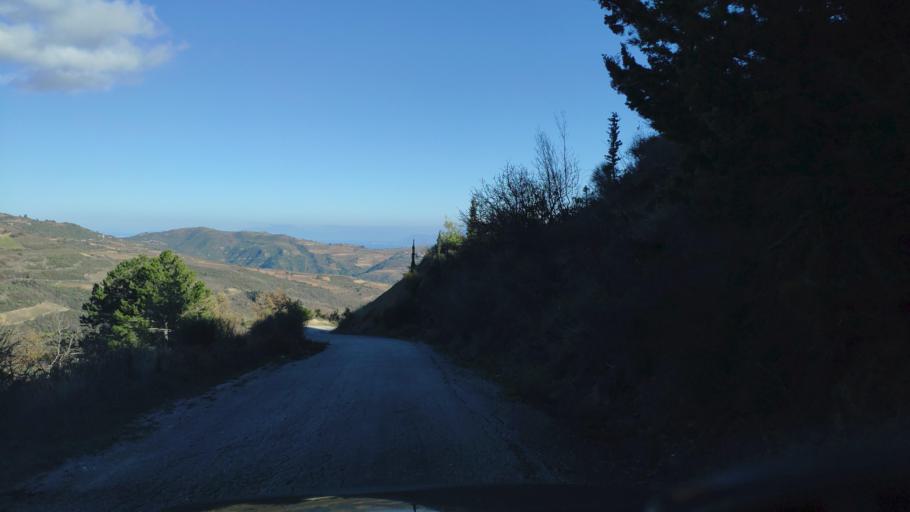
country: GR
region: Peloponnese
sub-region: Nomos Korinthias
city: Xylokastro
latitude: 38.0285
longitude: 22.4815
